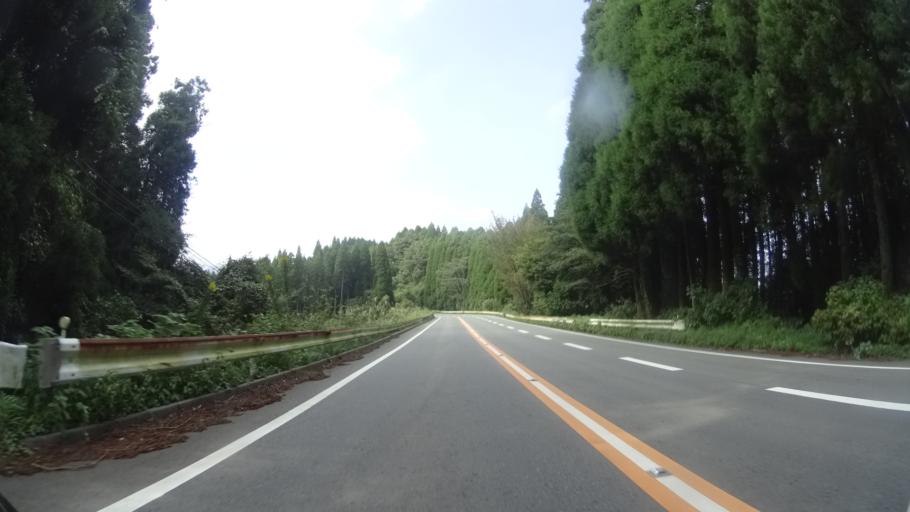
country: JP
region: Kumamoto
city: Aso
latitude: 33.0668
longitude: 131.0669
